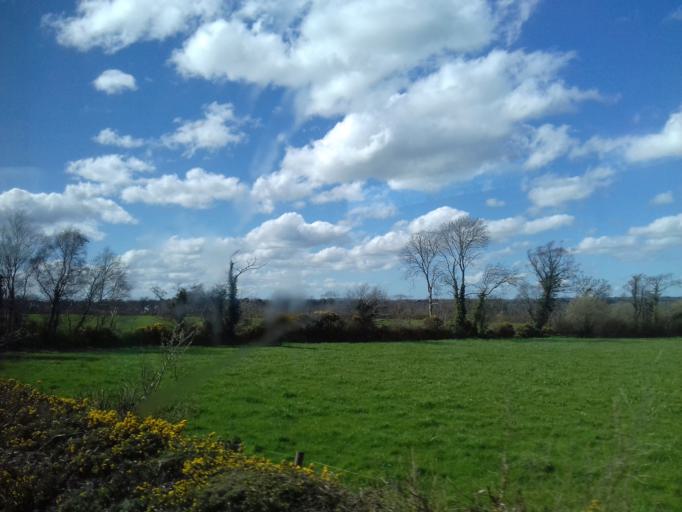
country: IE
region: Munster
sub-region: County Cork
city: Kanturk
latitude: 52.1293
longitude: -8.8379
